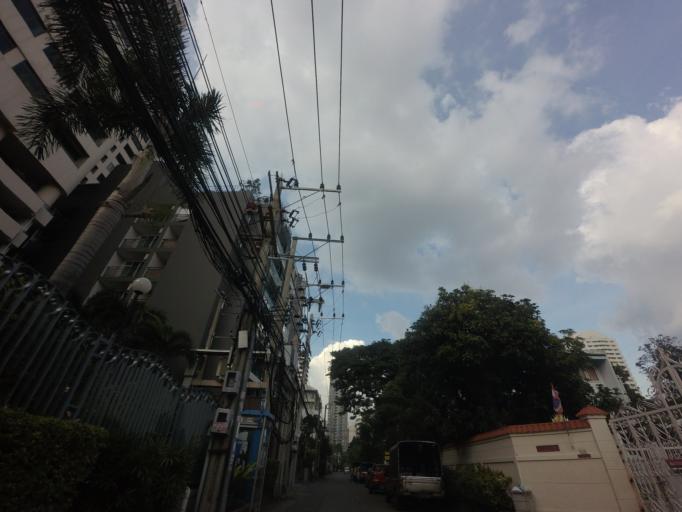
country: TH
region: Bangkok
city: Watthana
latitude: 13.7296
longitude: 100.5730
